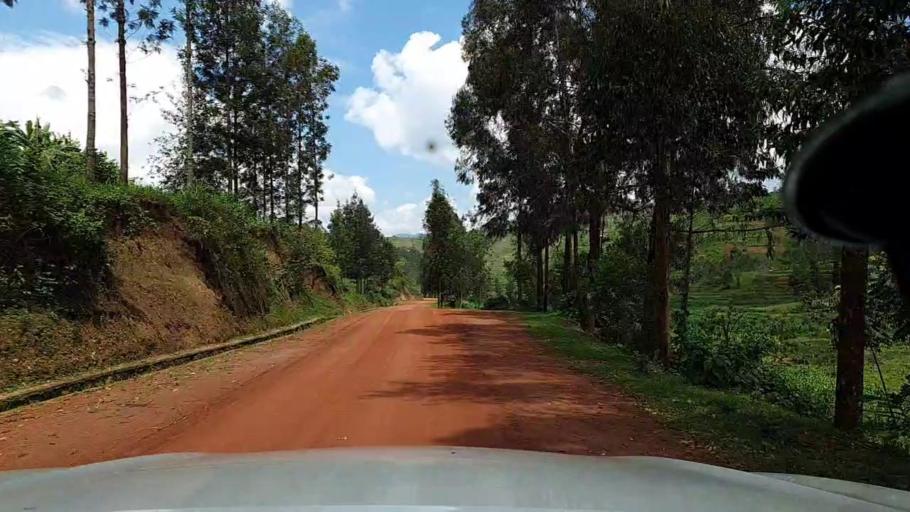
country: RW
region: Northern Province
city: Byumba
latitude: -1.7096
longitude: 29.8493
